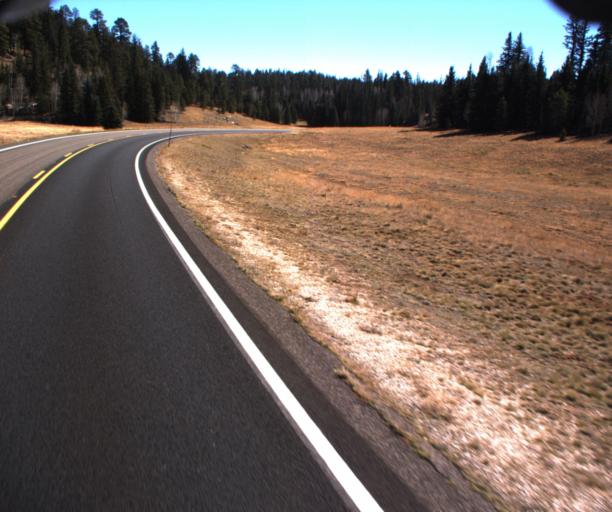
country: US
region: Arizona
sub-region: Coconino County
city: Grand Canyon
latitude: 36.5420
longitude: -112.1604
